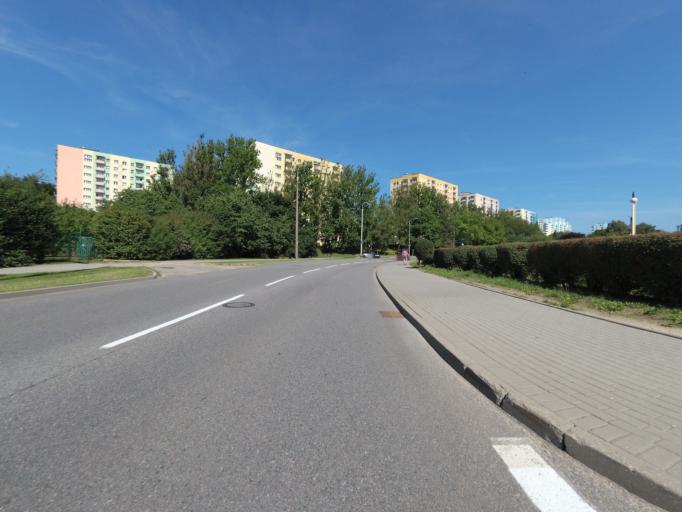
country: PL
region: Pomeranian Voivodeship
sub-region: Gdynia
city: Wielki Kack
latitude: 54.4929
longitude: 18.5080
